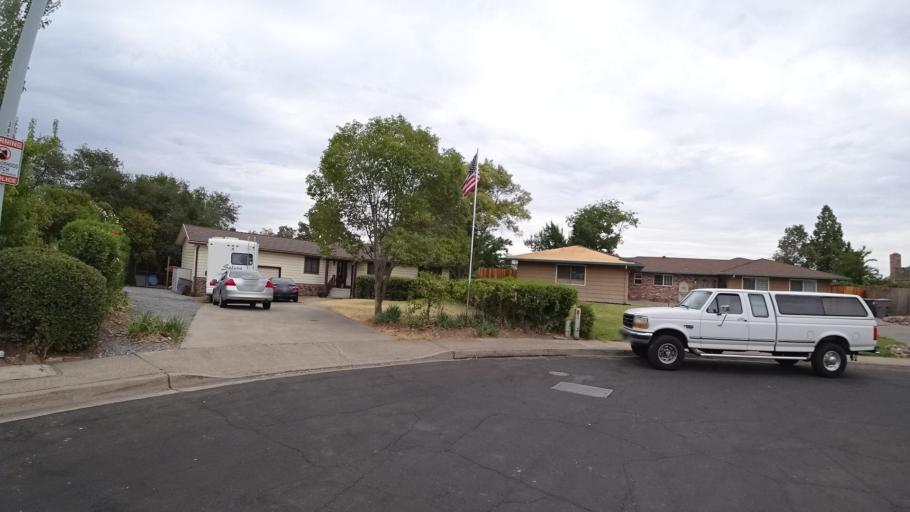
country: US
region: California
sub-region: Placer County
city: Rocklin
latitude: 38.7945
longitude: -121.2527
